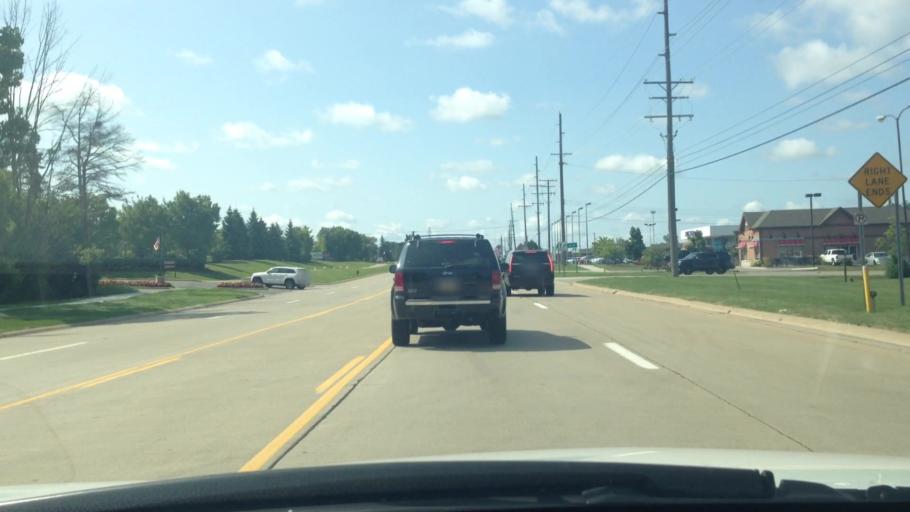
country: US
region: Michigan
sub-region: Oakland County
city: Wolverine Lake
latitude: 42.5584
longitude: -83.4393
